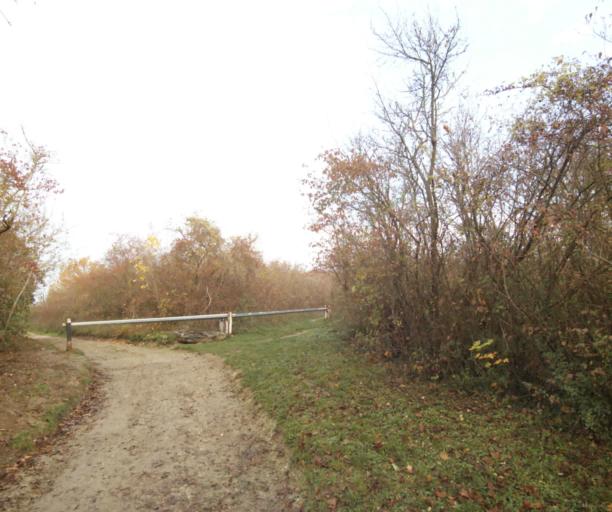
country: FR
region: Ile-de-France
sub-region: Departement des Yvelines
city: Triel-sur-Seine
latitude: 48.9950
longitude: 1.9896
